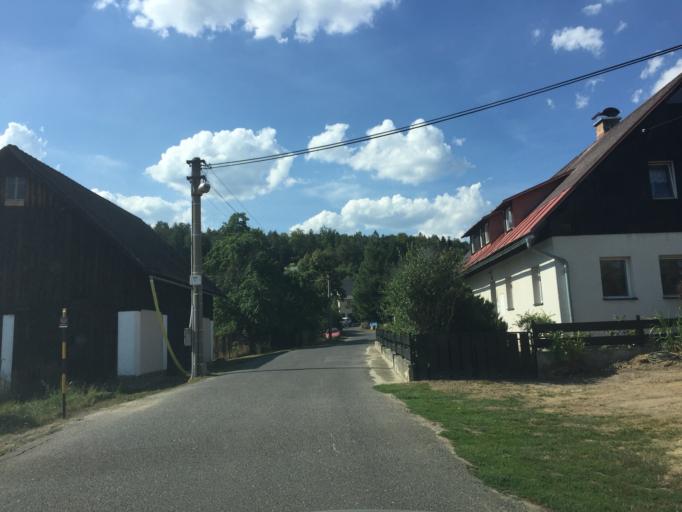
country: CZ
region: Liberecky
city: Mala Skala
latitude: 50.6263
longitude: 15.2113
